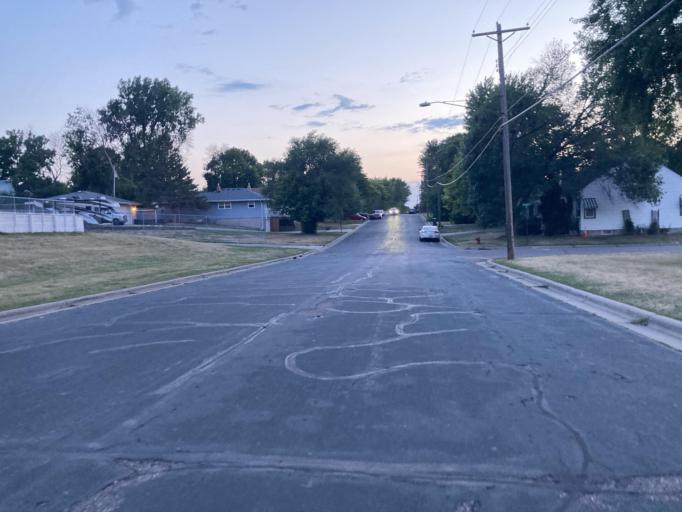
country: US
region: Minnesota
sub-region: Dakota County
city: West Saint Paul
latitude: 44.9178
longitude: -93.0712
